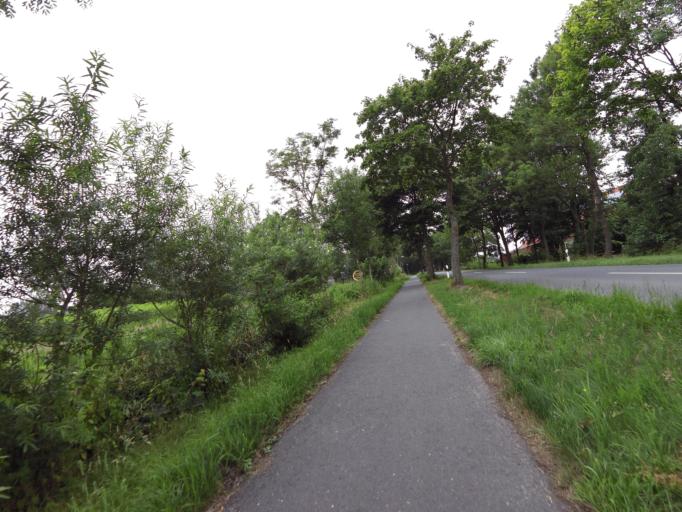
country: DE
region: Lower Saxony
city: Padingbuttel
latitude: 53.7081
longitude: 8.5550
